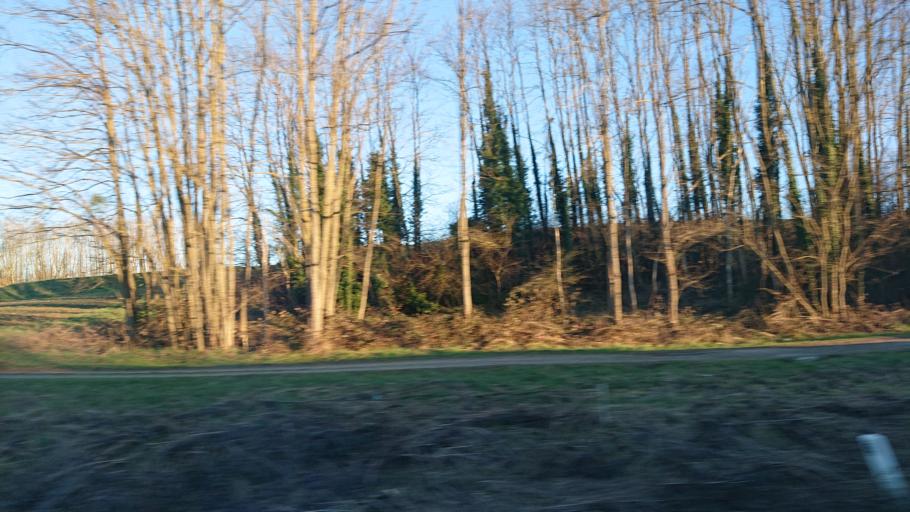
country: FR
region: Auvergne
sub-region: Departement de l'Allier
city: Saint-Germain-des-Fosses
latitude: 46.1910
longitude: 3.4259
